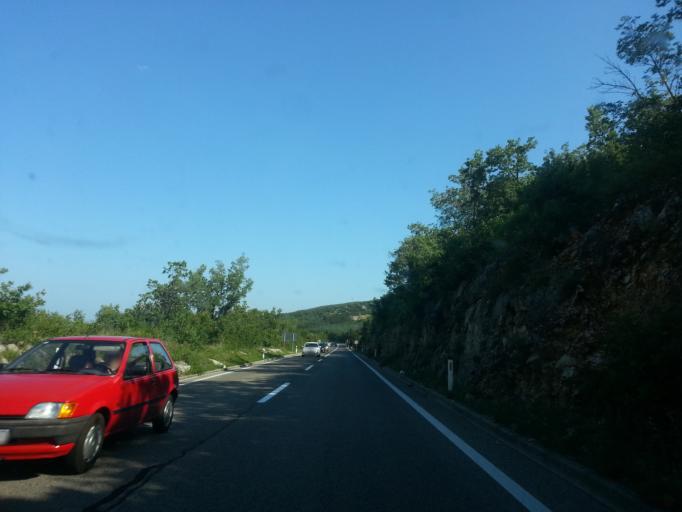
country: HR
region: Primorsko-Goranska
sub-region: Grad Crikvenica
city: Jadranovo
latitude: 45.2280
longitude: 14.6323
